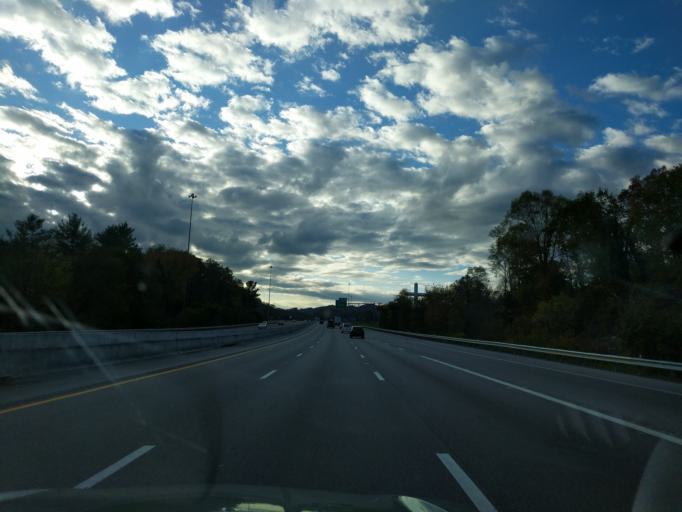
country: US
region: Tennessee
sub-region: Sullivan County
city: Fairmount
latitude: 36.6264
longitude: -82.1565
